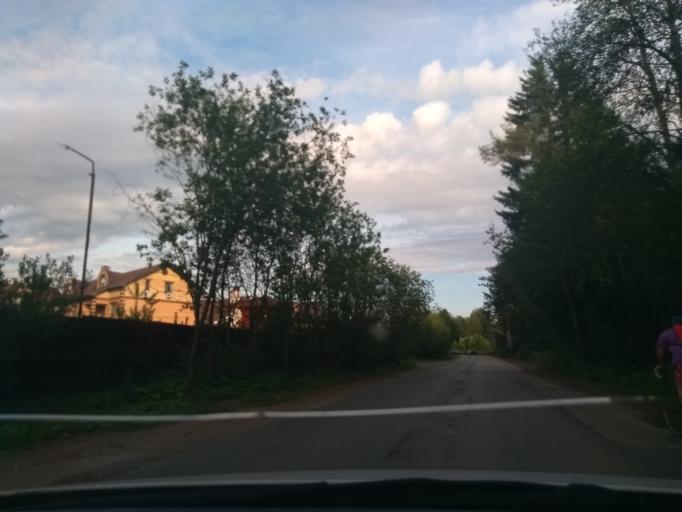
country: RU
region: Perm
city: Perm
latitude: 57.9970
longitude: 56.3312
